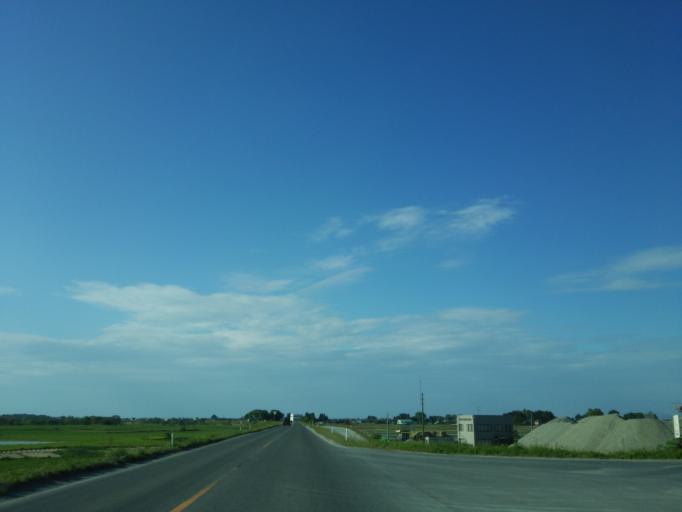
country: JP
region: Niigata
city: Gosen
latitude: 37.7923
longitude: 139.1840
